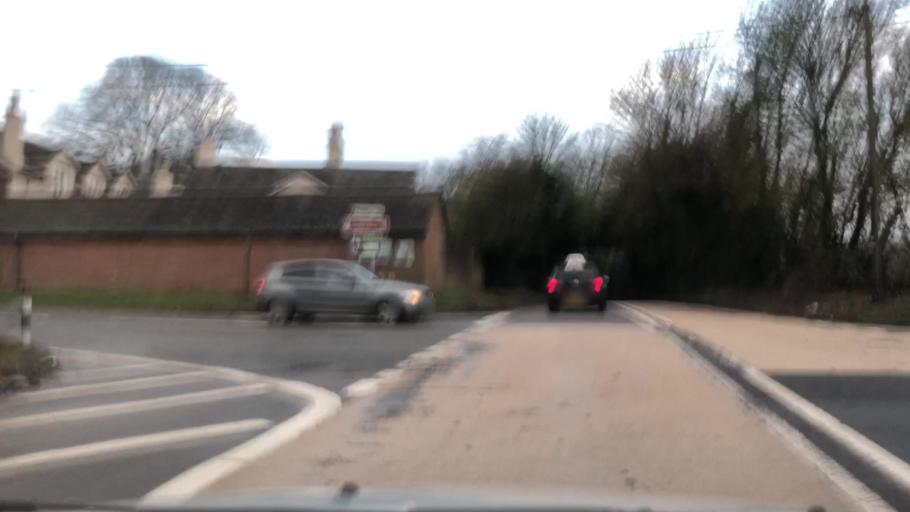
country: GB
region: England
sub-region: Hampshire
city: Alton
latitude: 51.1845
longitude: -0.9881
